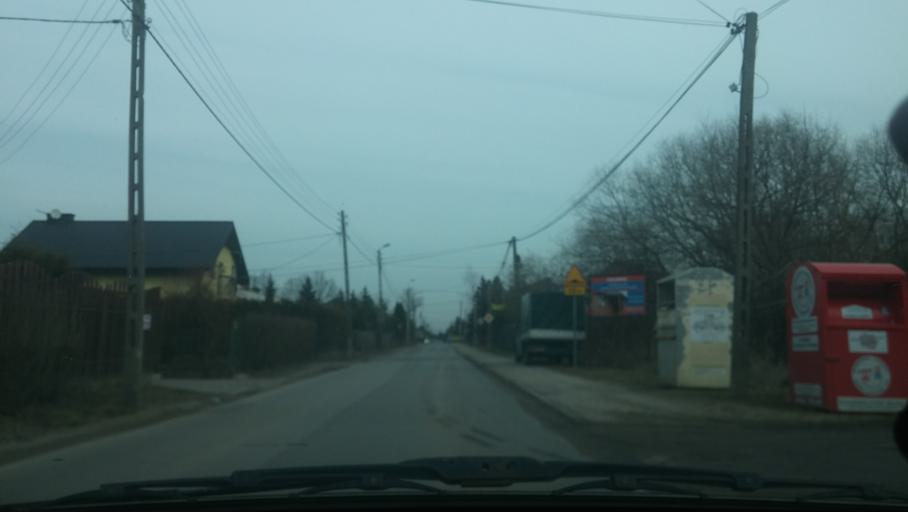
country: PL
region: Masovian Voivodeship
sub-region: Powiat wolominski
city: Marki
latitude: 52.3100
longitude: 21.1077
